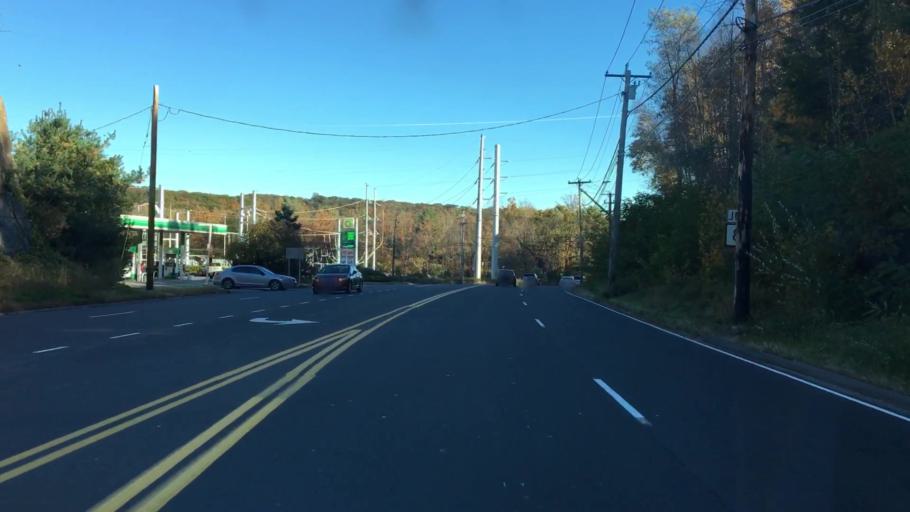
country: US
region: Connecticut
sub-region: Fairfield County
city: Shelton
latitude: 41.2762
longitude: -73.1201
